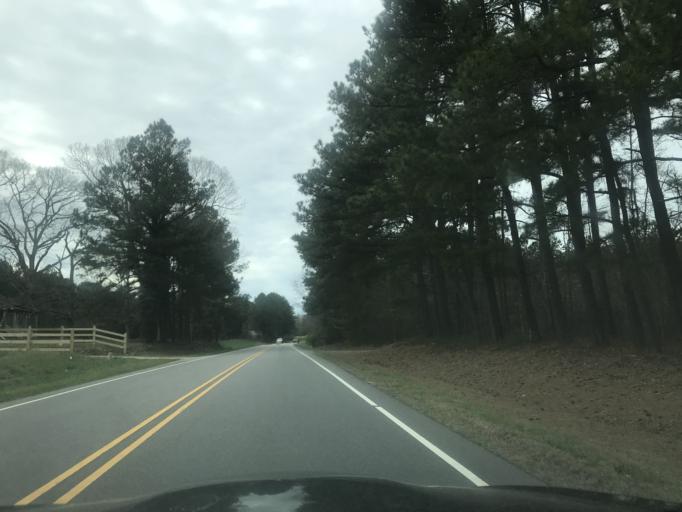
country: US
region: North Carolina
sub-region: Franklin County
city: Louisburg
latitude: 36.0825
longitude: -78.3432
